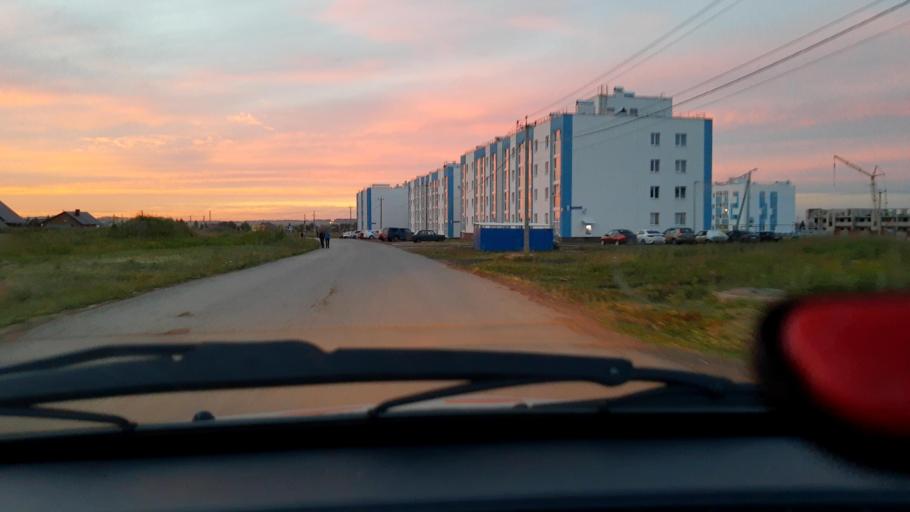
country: RU
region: Bashkortostan
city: Avdon
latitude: 54.4838
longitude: 55.8804
